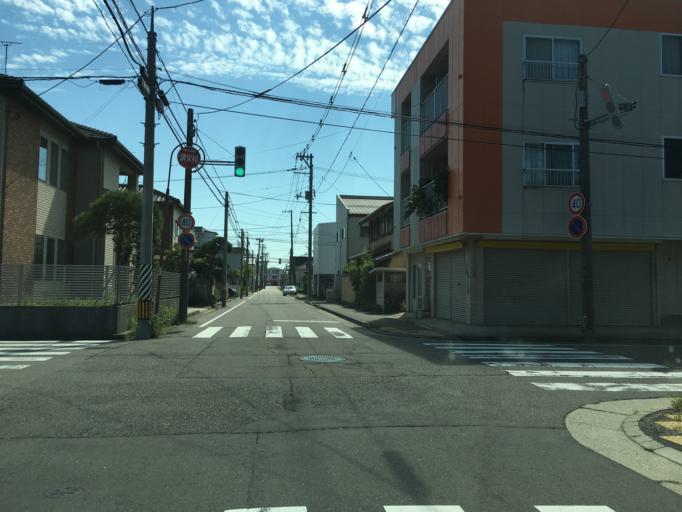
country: JP
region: Niigata
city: Niigata-shi
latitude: 37.9126
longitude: 139.0234
